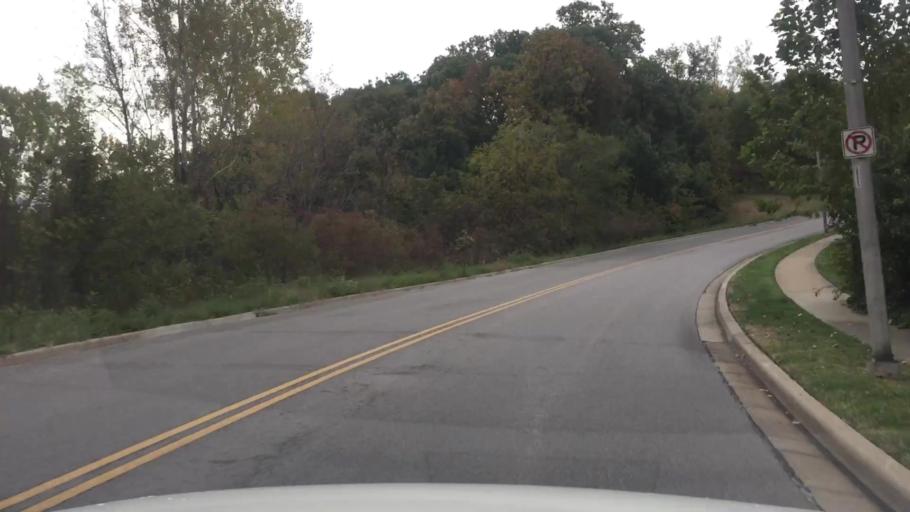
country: US
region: Kansas
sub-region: Johnson County
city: Shawnee
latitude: 39.0240
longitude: -94.7428
